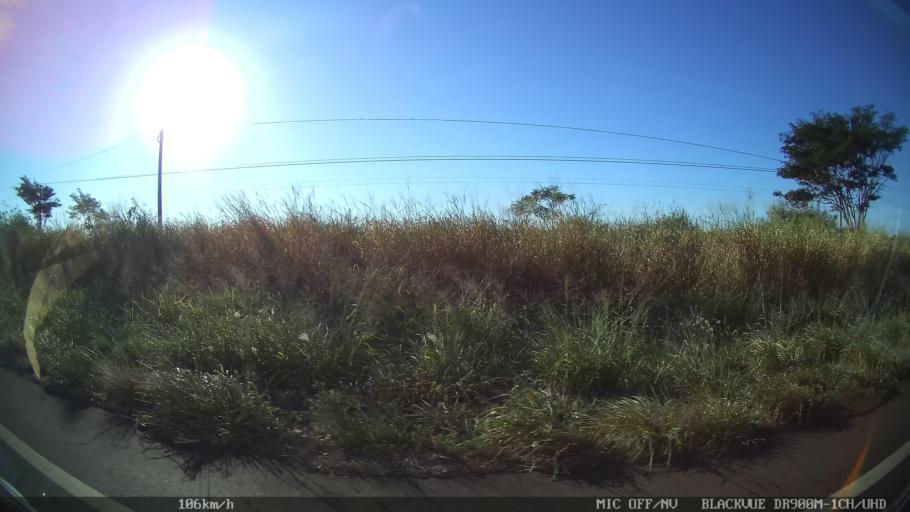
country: BR
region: Sao Paulo
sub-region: Olimpia
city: Olimpia
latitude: -20.7348
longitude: -49.0728
